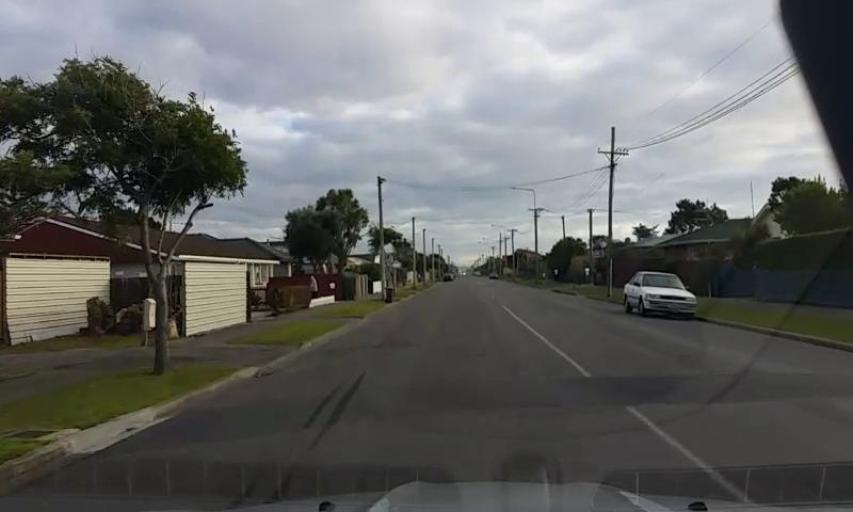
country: NZ
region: Canterbury
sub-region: Christchurch City
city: Christchurch
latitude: -43.5341
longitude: 172.7373
